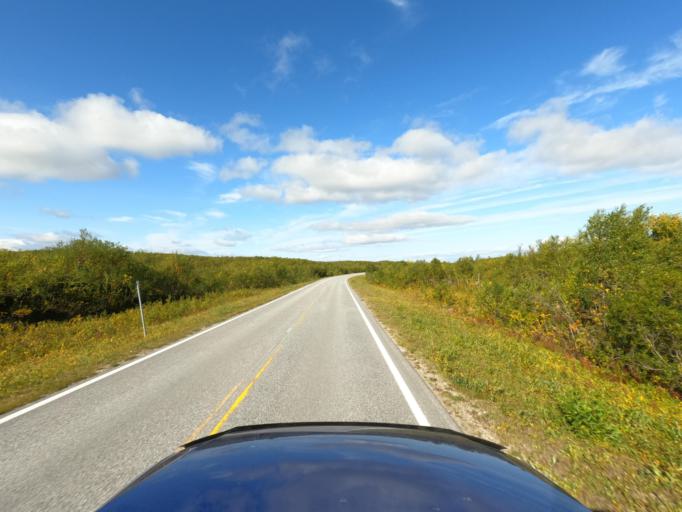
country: NO
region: Finnmark Fylke
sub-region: Karasjok
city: Karasjohka
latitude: 69.5942
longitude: 25.3323
